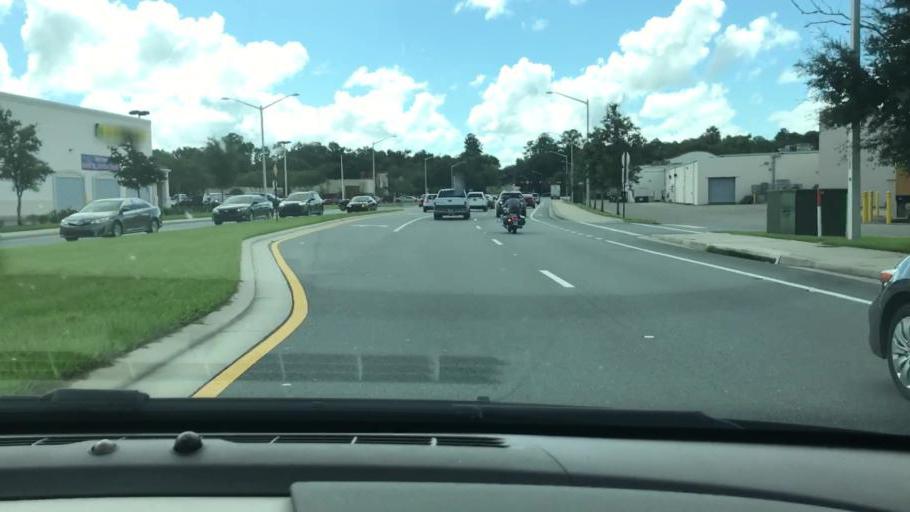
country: US
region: Florida
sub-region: Alachua County
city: Gainesville
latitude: 29.6227
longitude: -82.3819
